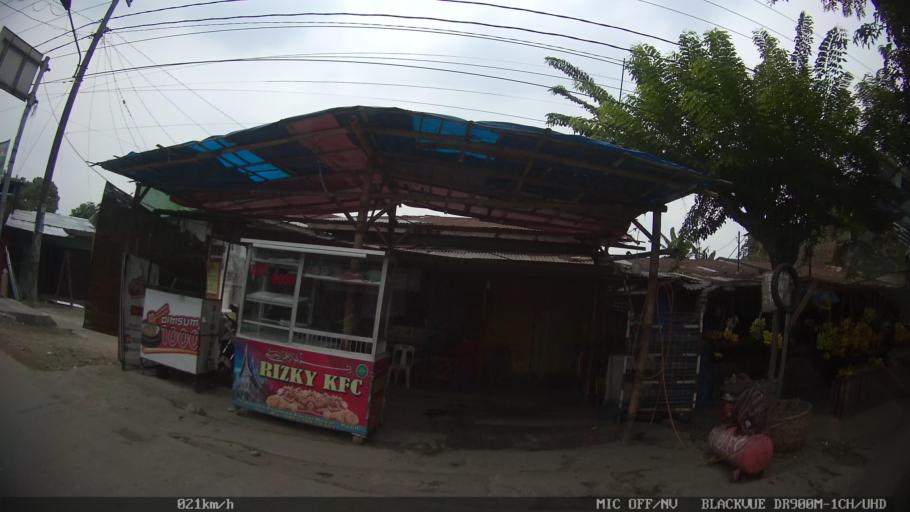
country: ID
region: North Sumatra
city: Medan
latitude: 3.5813
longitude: 98.7287
